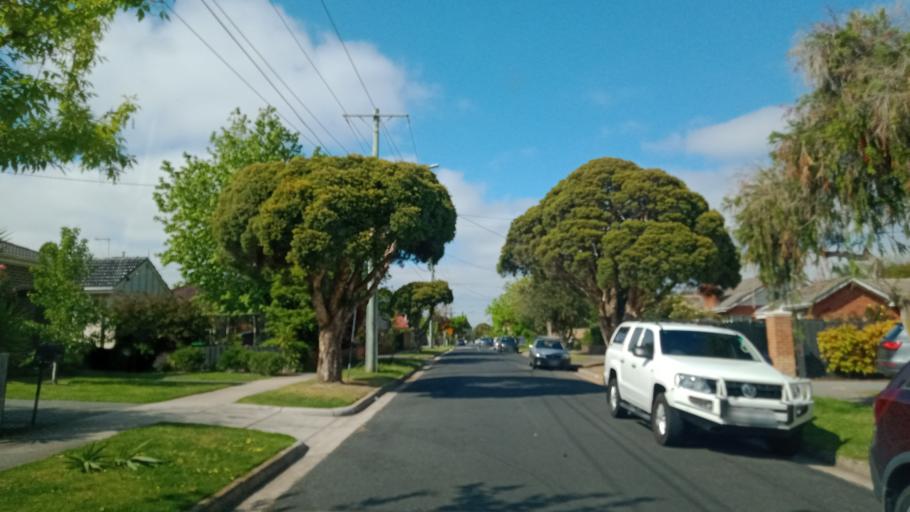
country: AU
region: Victoria
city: Hughesdale
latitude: -37.9139
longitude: 145.0792
